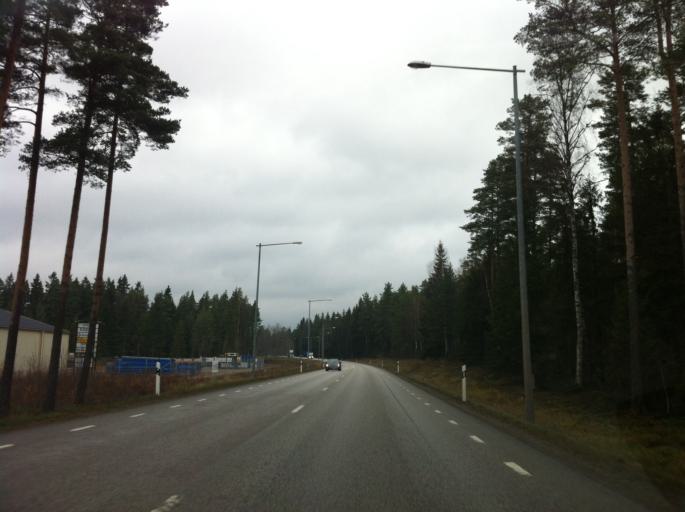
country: SE
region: Joenkoeping
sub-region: Vetlanda Kommun
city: Vetlanda
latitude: 57.4135
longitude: 15.0612
